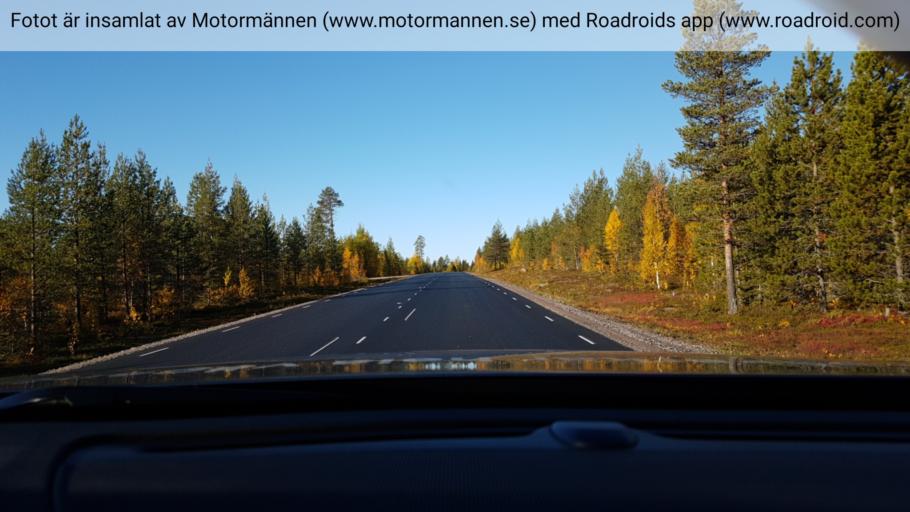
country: SE
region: Vaesterbotten
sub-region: Norsjo Kommun
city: Norsjoe
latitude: 65.4106
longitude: 19.8002
